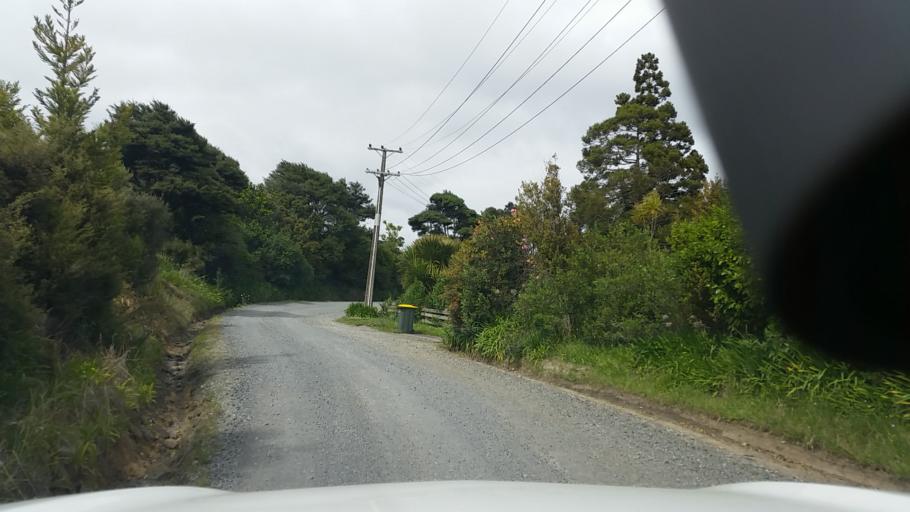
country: NZ
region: Auckland
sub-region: Auckland
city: Muriwai Beach
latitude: -36.8461
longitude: 174.5229
